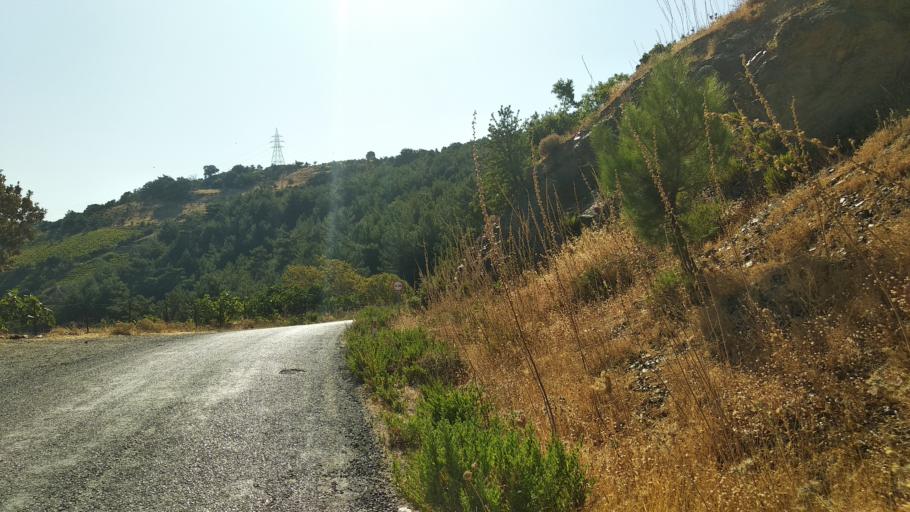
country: TR
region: Izmir
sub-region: Seferihisar
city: Seferhisar
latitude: 38.3298
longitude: 26.9454
